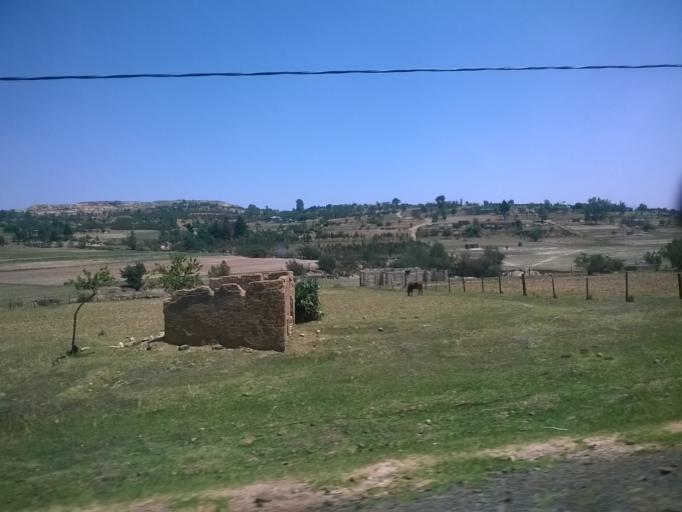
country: LS
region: Berea
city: Teyateyaneng
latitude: -29.1066
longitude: 27.8338
